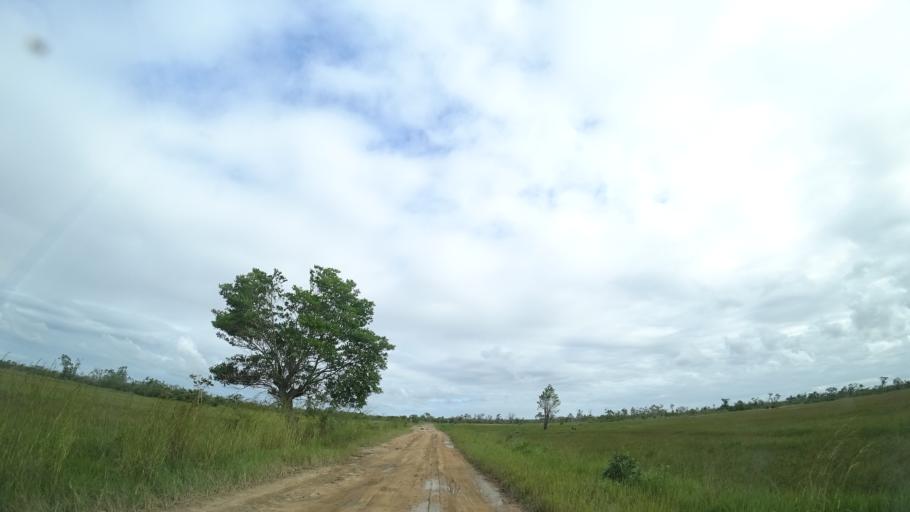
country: MZ
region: Sofala
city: Dondo
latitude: -19.5876
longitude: 35.0861
